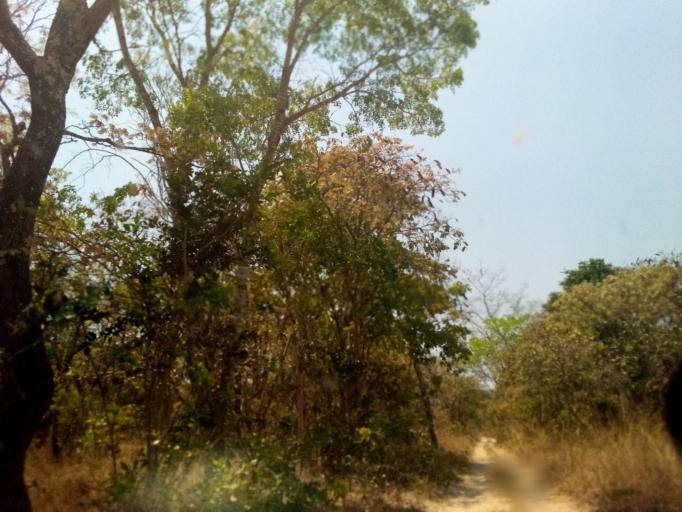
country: ZM
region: Copperbelt
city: Kataba
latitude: -12.2532
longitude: 30.3884
